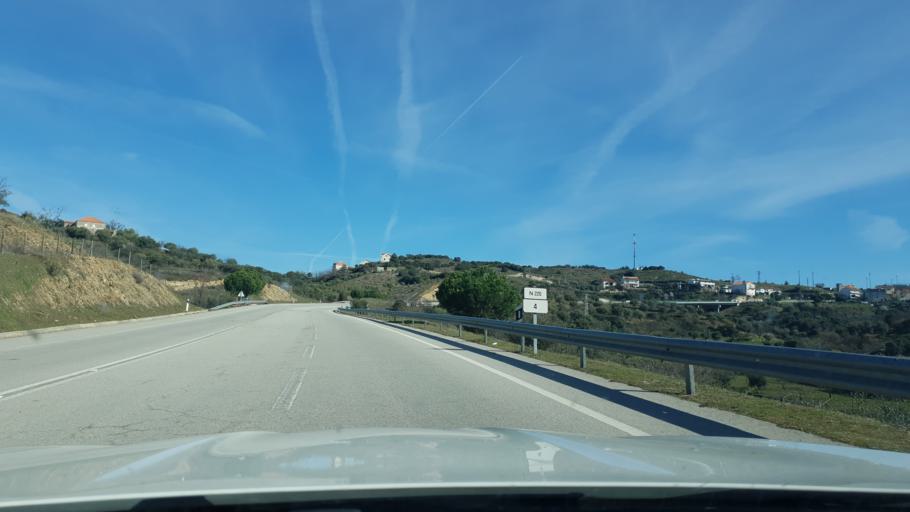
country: PT
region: Braganca
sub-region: Torre de Moncorvo
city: Torre de Moncorvo
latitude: 41.1779
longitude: -7.0628
